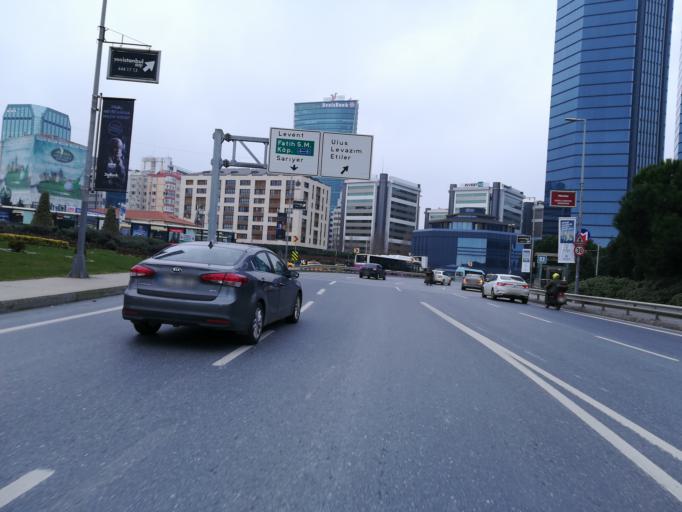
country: TR
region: Istanbul
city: Sisli
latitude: 41.0671
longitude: 29.0145
